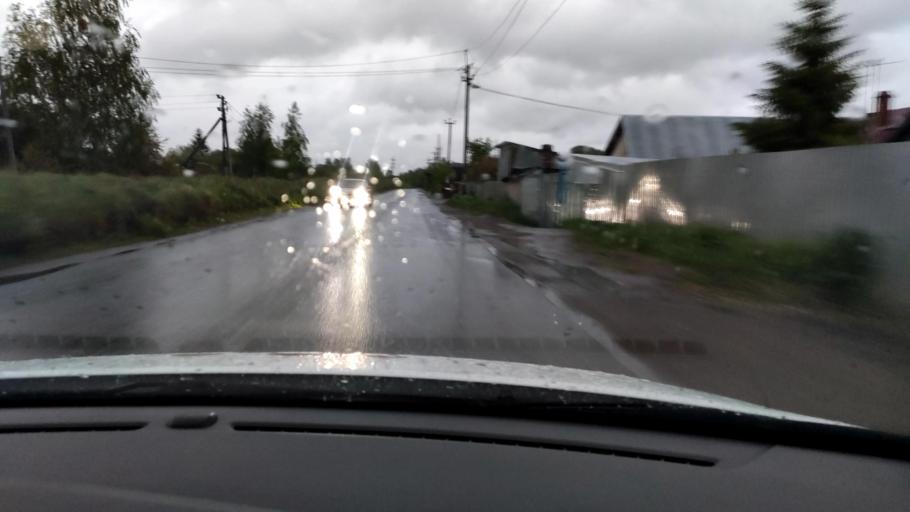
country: RU
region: Tatarstan
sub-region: Gorod Kazan'
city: Kazan
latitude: 55.7230
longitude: 49.1132
